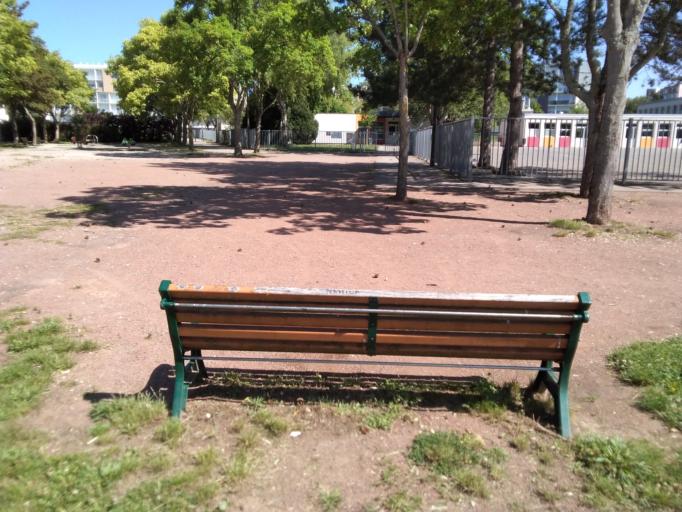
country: FR
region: Picardie
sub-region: Departement de la Somme
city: Rivery
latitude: 49.9103
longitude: 2.3239
